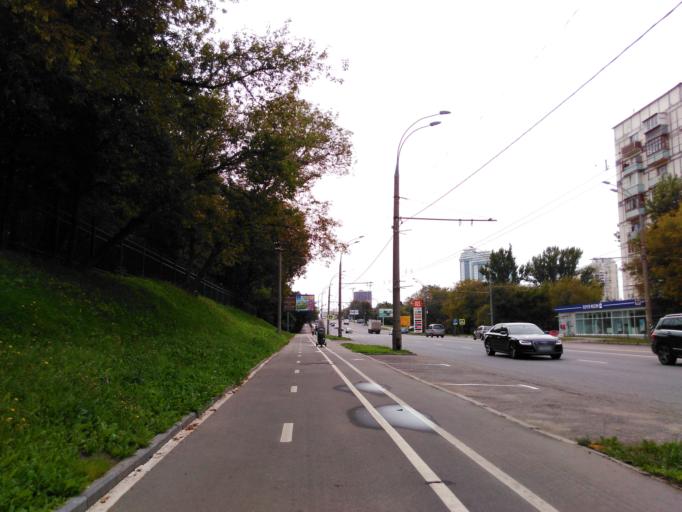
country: RU
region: Moscow
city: Vorob'yovo
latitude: 55.7199
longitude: 37.5235
